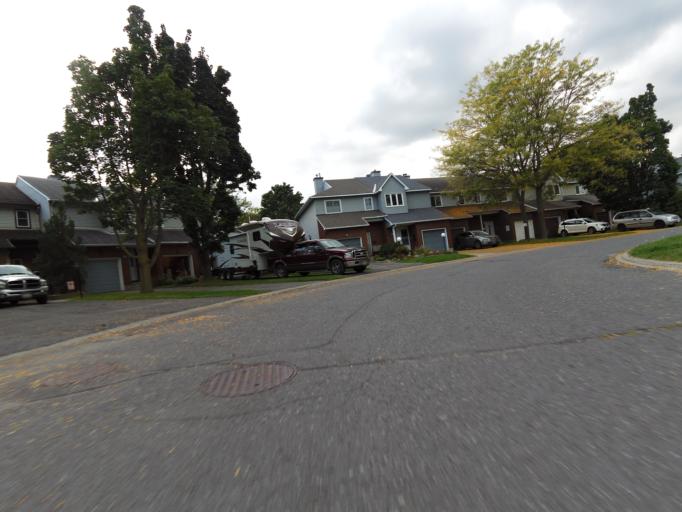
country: CA
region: Ontario
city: Bells Corners
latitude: 45.2631
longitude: -75.7642
